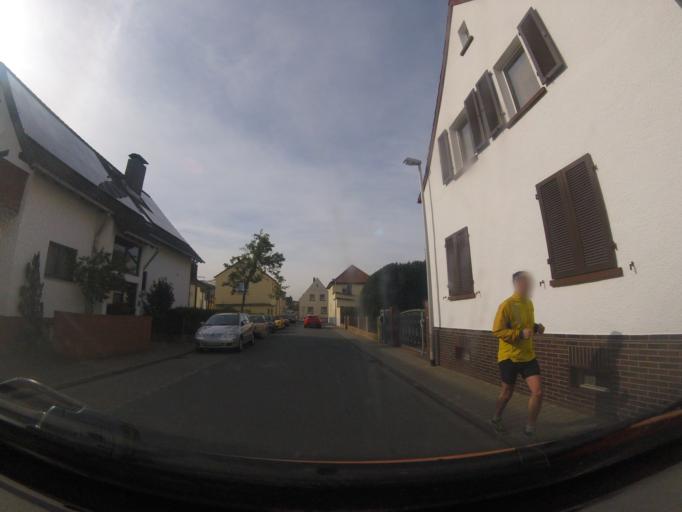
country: DE
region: Hesse
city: Griesheim
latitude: 49.8596
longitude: 8.5645
